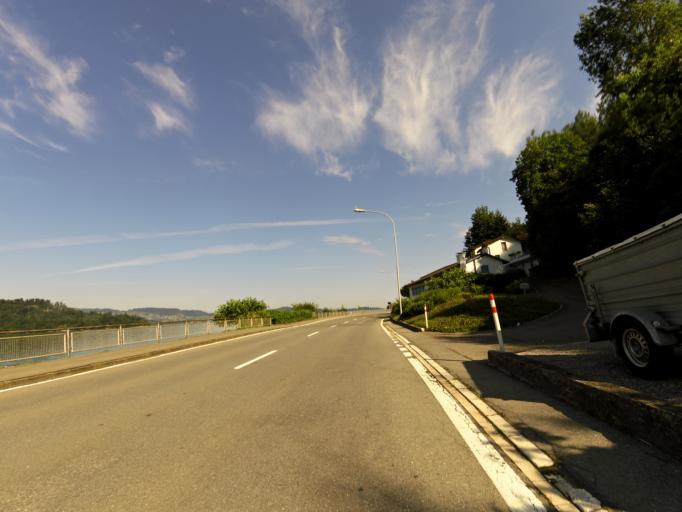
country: CH
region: Zug
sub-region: Zug
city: Walchwil
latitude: 47.1114
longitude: 8.5021
